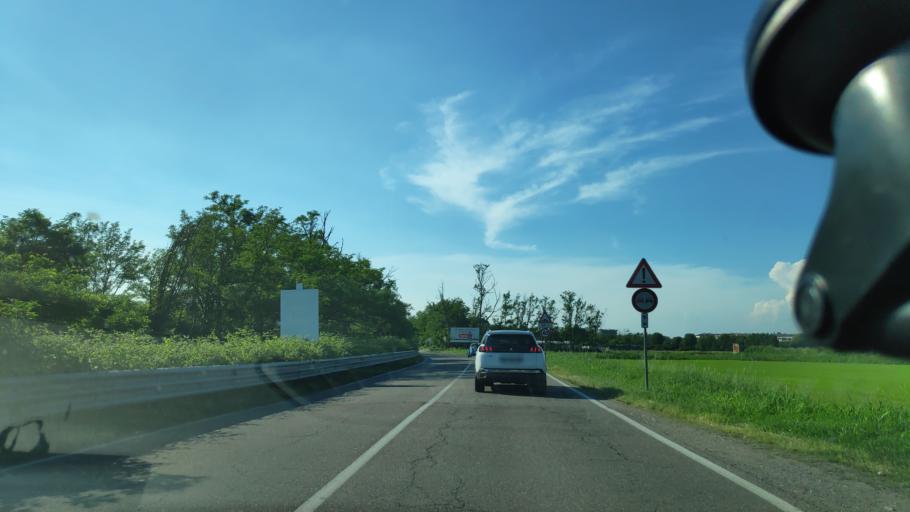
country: IT
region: Lombardy
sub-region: Citta metropolitana di Milano
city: Basiglio
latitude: 45.3671
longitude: 9.1521
